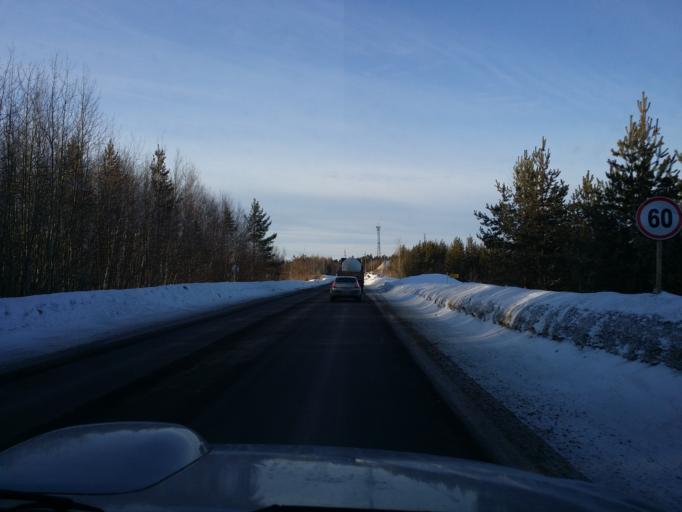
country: RU
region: Khanty-Mansiyskiy Avtonomnyy Okrug
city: Izluchinsk
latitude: 60.9624
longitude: 76.8509
